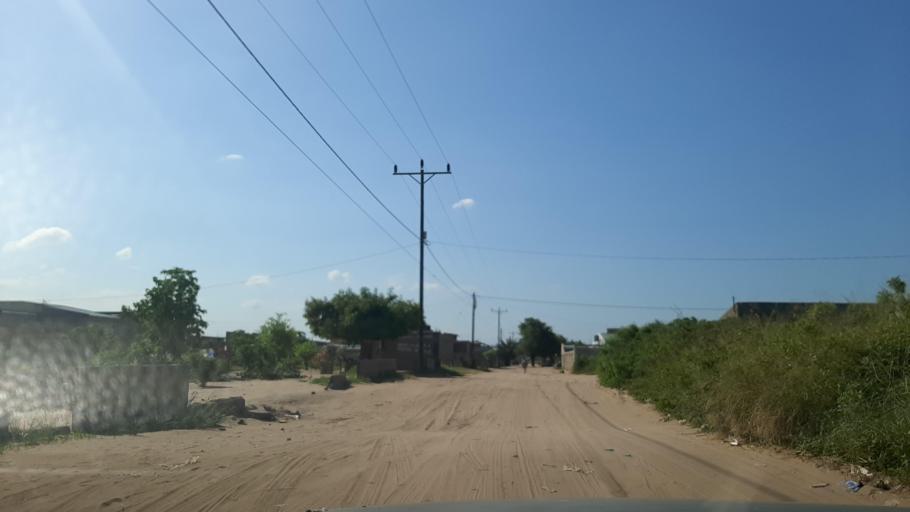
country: MZ
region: Maputo
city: Matola
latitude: -25.8080
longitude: 32.4917
